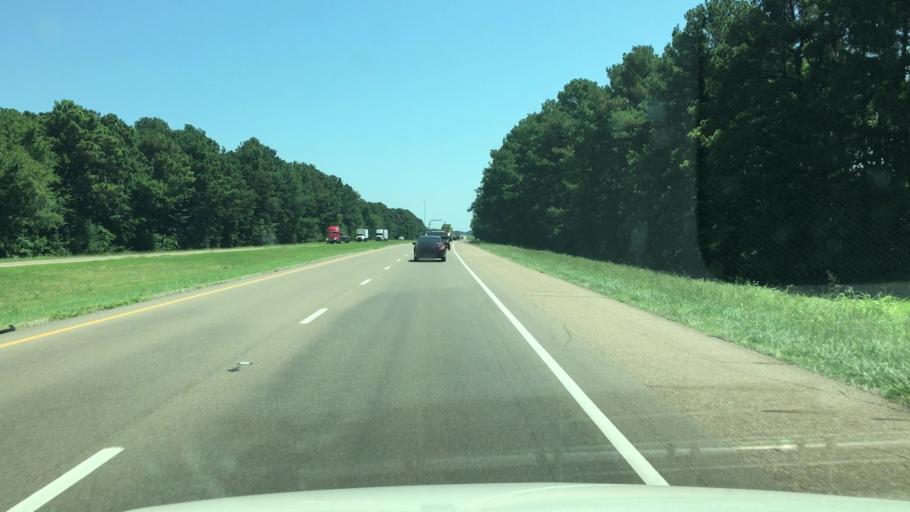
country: US
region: Texas
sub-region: Bowie County
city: New Boston
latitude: 33.4580
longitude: -94.4853
